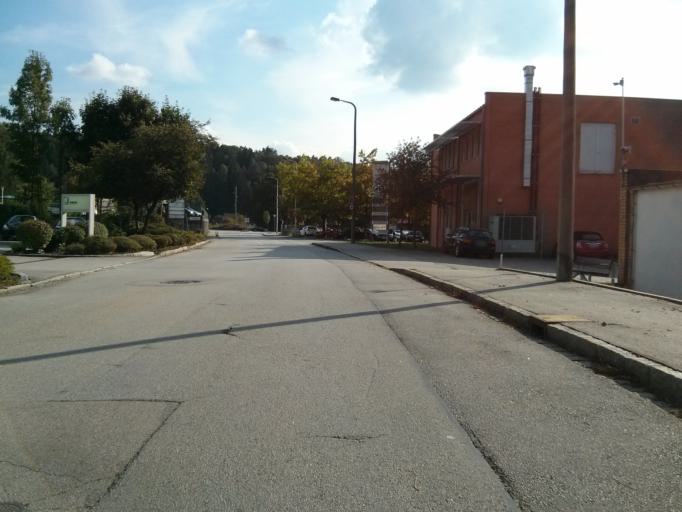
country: DE
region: Bavaria
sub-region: Lower Bavaria
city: Deggendorf
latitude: 48.8509
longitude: 12.9839
